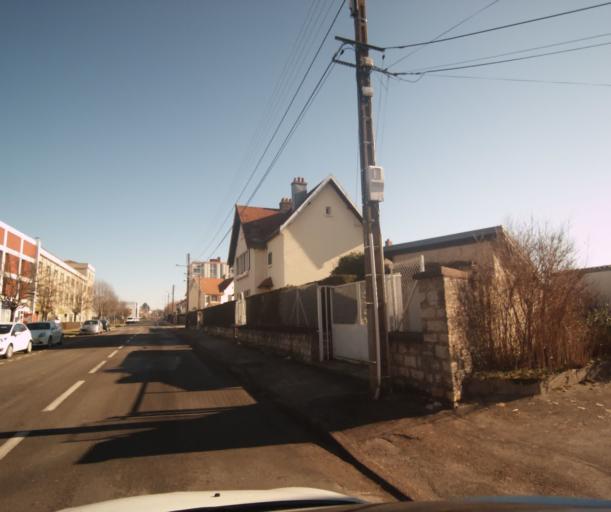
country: FR
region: Franche-Comte
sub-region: Departement du Doubs
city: Besancon
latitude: 47.2409
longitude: 6.0061
